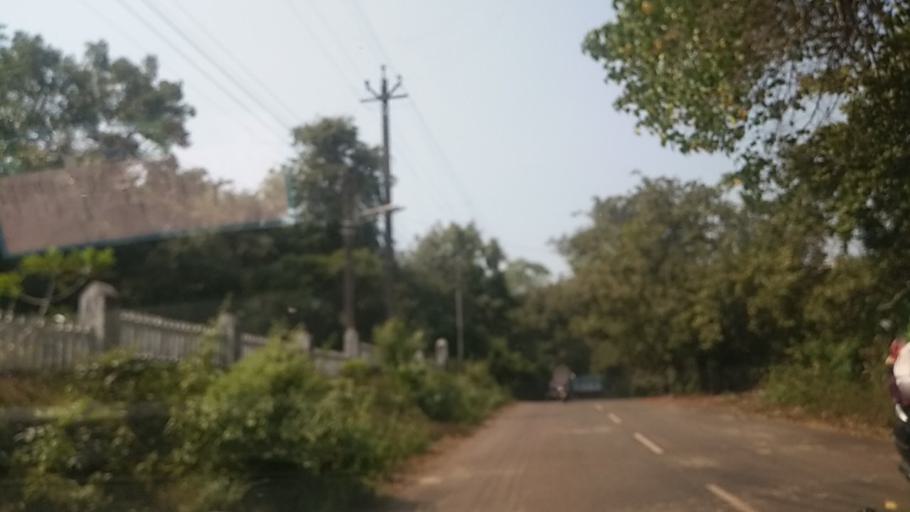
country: IN
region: Goa
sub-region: North Goa
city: Mapuca
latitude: 15.6154
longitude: 73.7965
